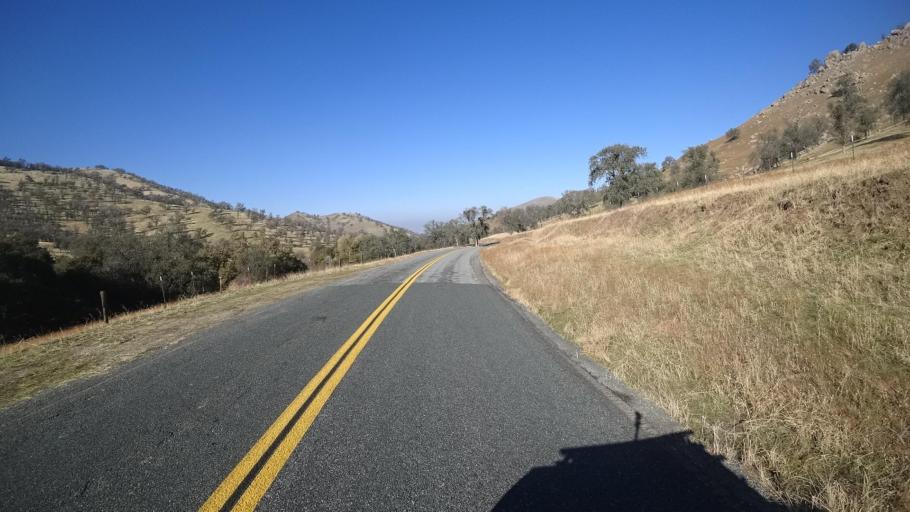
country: US
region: California
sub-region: Kern County
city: Alta Sierra
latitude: 35.7925
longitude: -118.8071
